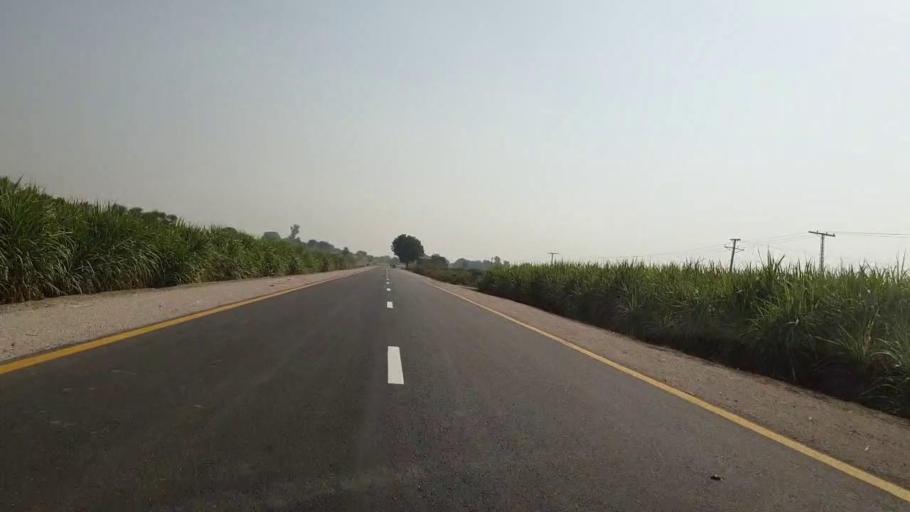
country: PK
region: Sindh
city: Bhan
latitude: 26.6068
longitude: 67.7790
